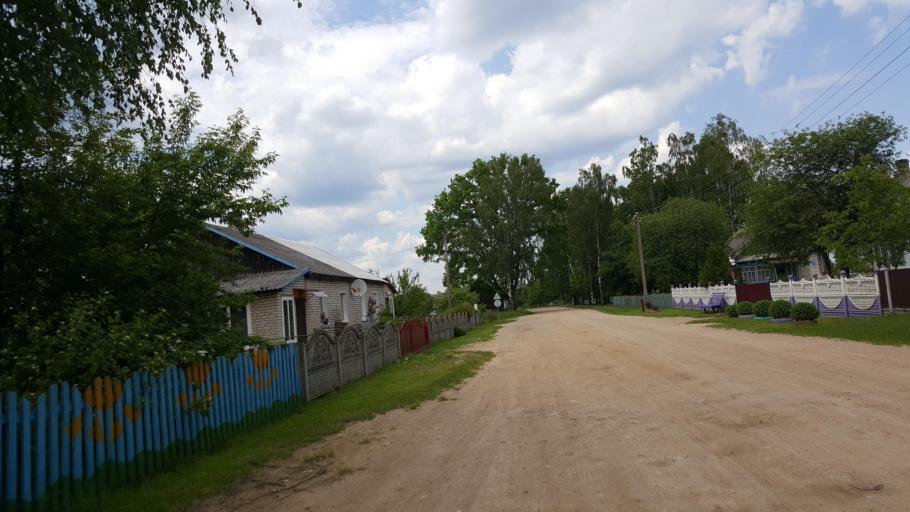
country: PL
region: Podlasie
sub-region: Powiat hajnowski
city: Bialowieza
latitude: 52.6696
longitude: 24.0855
